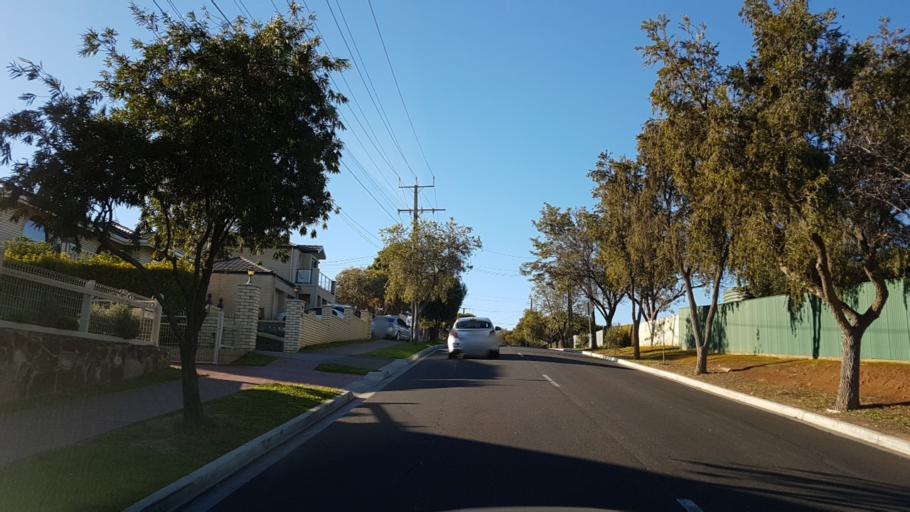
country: AU
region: South Australia
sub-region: Campbelltown
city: Hectorville
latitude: -34.8806
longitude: 138.6554
